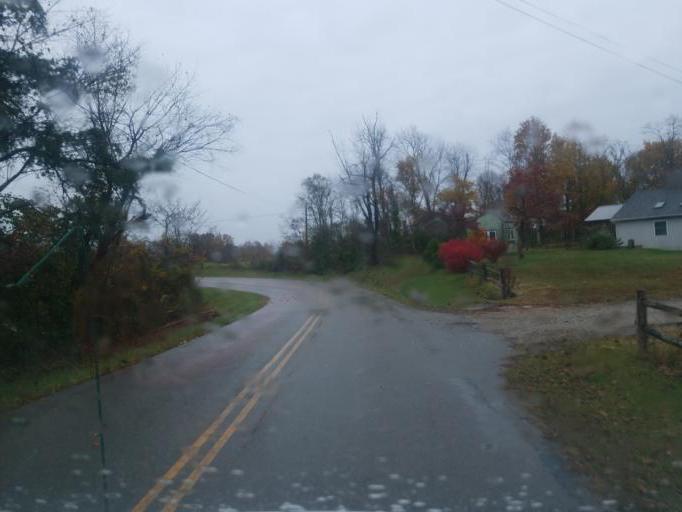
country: US
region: Ohio
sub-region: Washington County
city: Beverly
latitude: 39.4533
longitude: -81.6164
